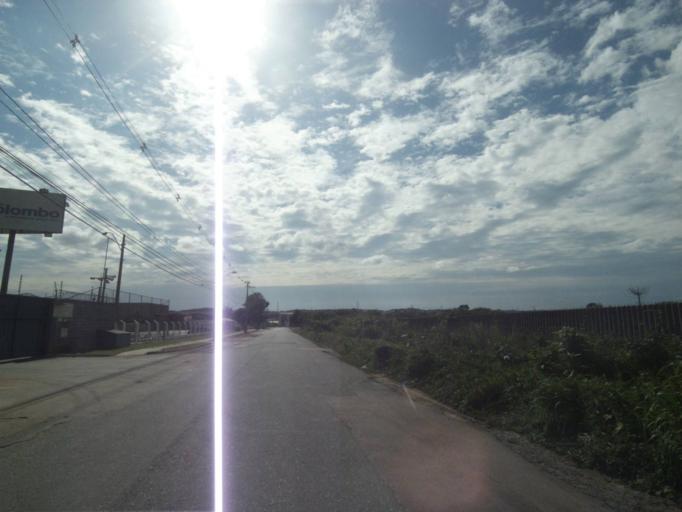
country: BR
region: Parana
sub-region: Curitiba
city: Curitiba
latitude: -25.5041
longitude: -49.3328
